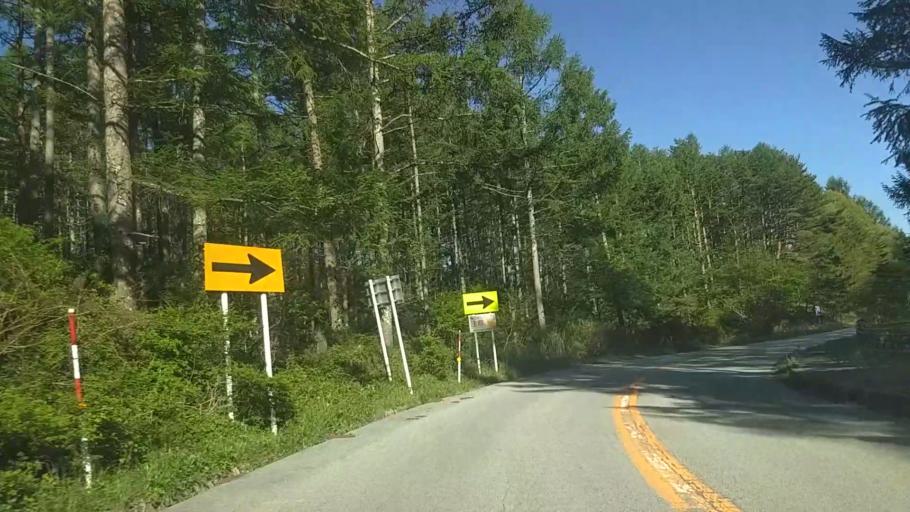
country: JP
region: Nagano
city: Chino
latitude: 35.9001
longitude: 138.3548
